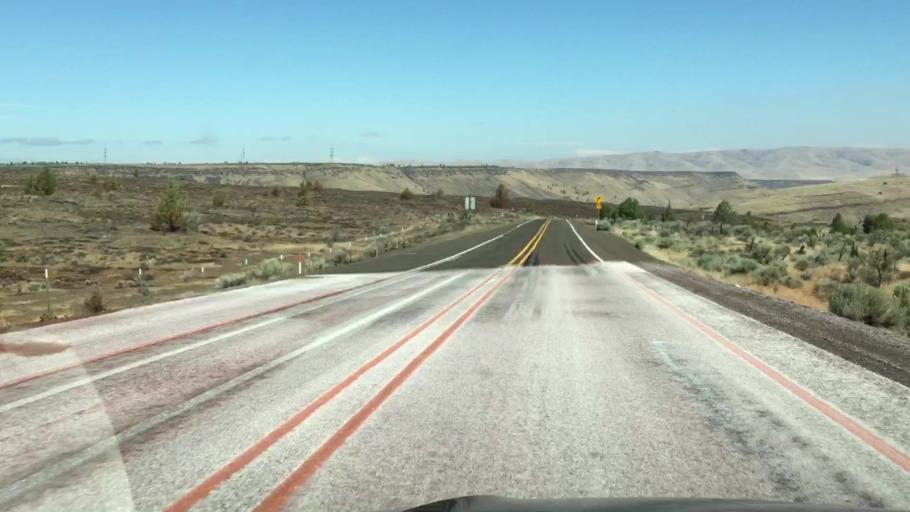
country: US
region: Oregon
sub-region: Jefferson County
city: Warm Springs
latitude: 45.1611
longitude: -121.0716
